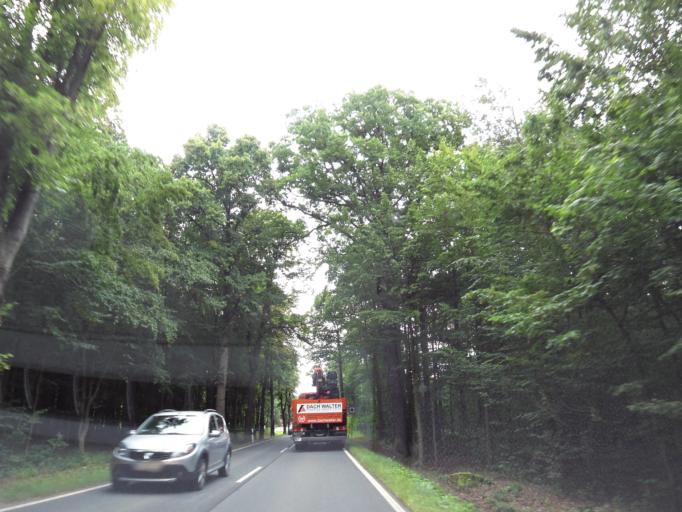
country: DE
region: Thuringia
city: Weissenborn
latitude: 50.9567
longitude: 11.8781
